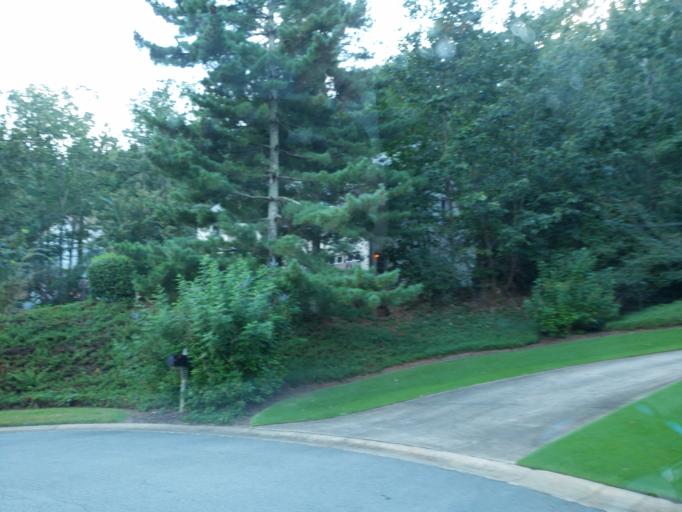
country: US
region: Georgia
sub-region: Cherokee County
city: Woodstock
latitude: 34.0578
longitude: -84.4517
